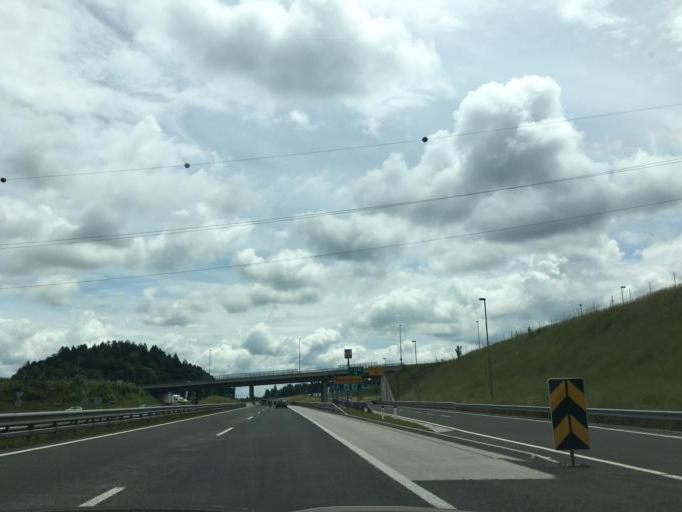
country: SI
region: Radovljica
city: Radovljica
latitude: 46.3419
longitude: 14.1876
